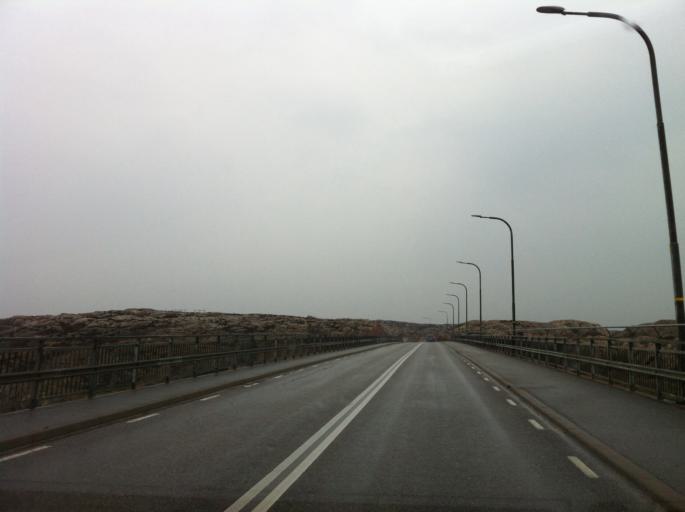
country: SE
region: Vaestra Goetaland
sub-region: Sotenas Kommun
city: Kungshamn
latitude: 58.3649
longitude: 11.2425
